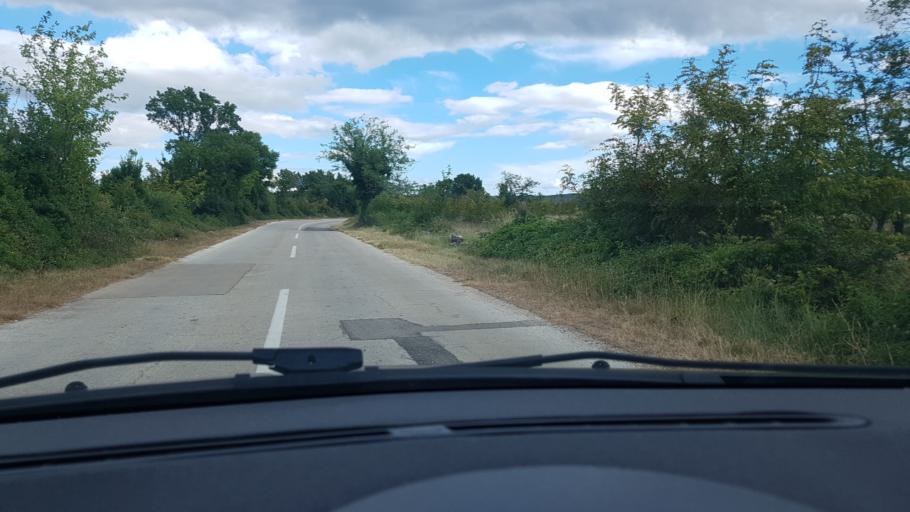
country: HR
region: Sibensko-Kniniska
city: Kistanje
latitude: 44.1072
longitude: 15.9402
